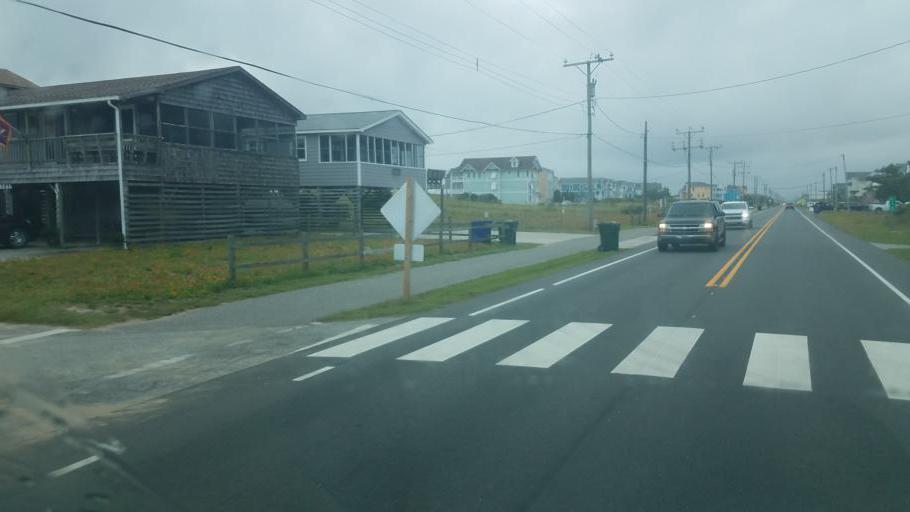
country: US
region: North Carolina
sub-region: Dare County
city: Nags Head
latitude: 35.9926
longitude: -75.6446
